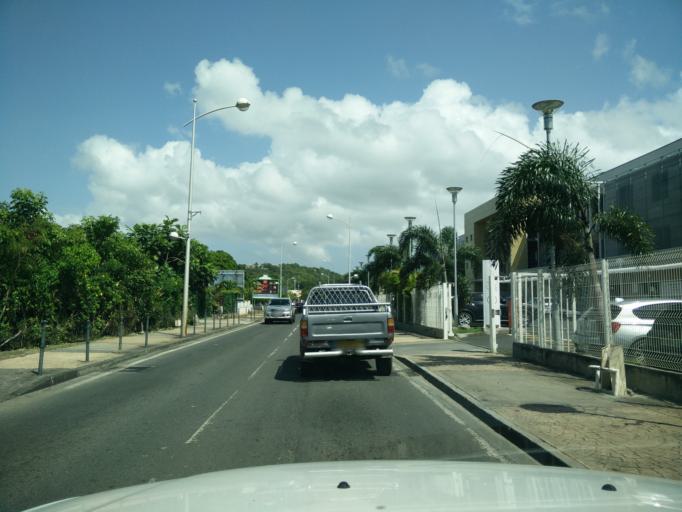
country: GP
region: Guadeloupe
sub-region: Guadeloupe
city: Le Gosier
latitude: 16.2131
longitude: -61.5005
